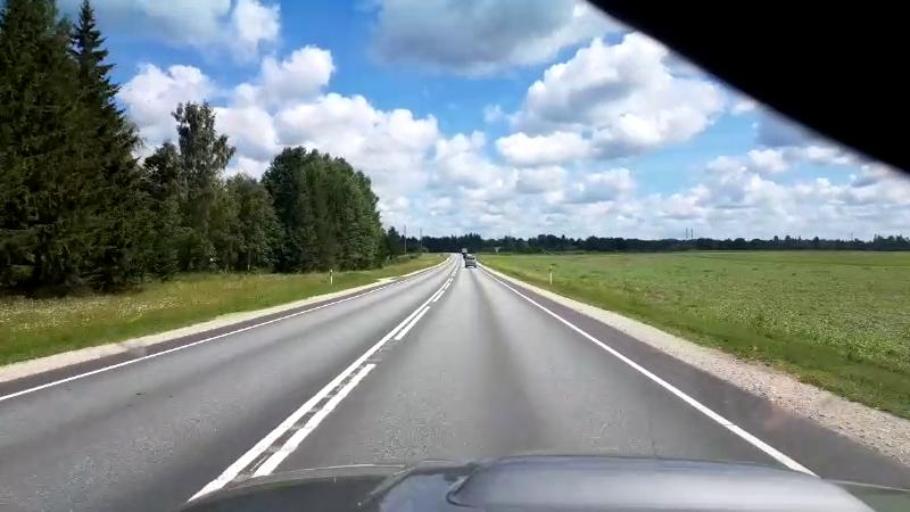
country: EE
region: Laeaene-Virumaa
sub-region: Tapa vald
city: Tapa
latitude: 59.2663
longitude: 26.0264
